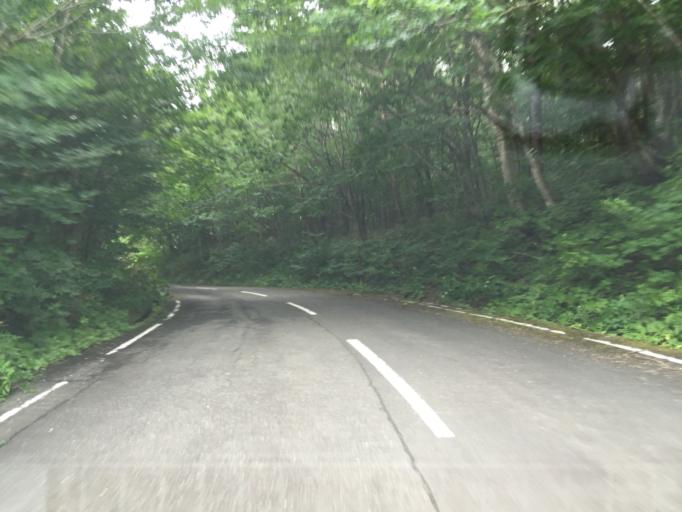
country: JP
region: Fukushima
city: Nihommatsu
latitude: 37.6535
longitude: 140.3053
